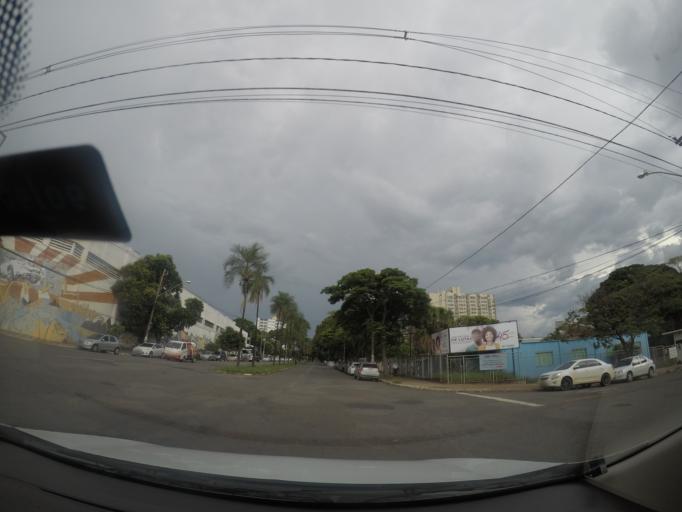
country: BR
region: Goias
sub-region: Goiania
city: Goiania
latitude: -16.6717
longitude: -49.2443
